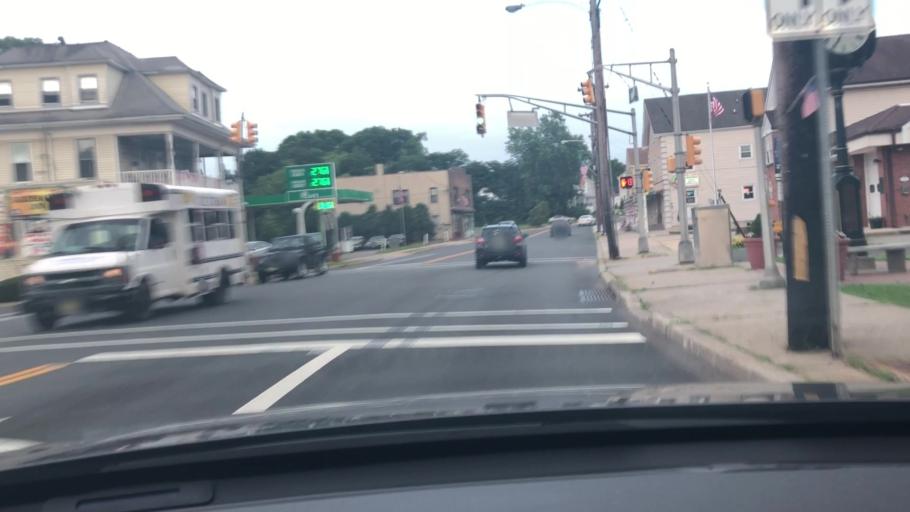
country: US
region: New Jersey
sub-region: Middlesex County
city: Milltown
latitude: 40.4508
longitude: -74.4363
